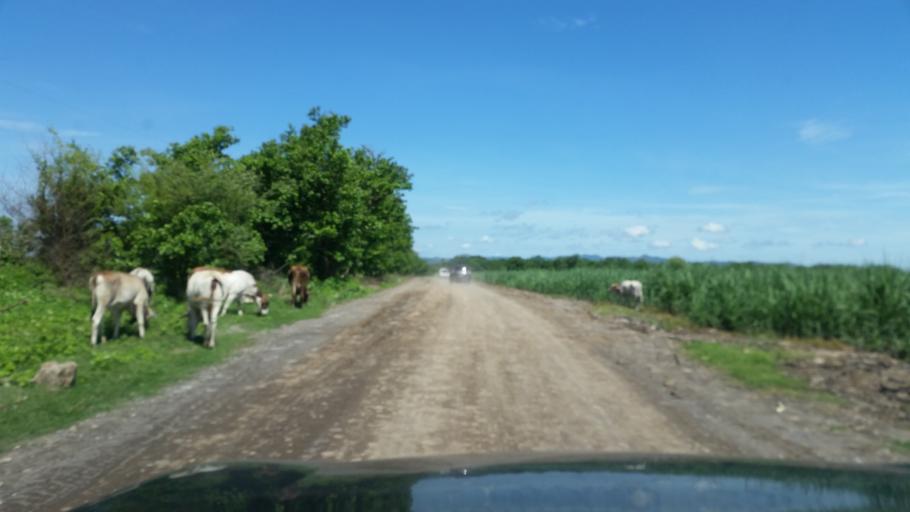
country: NI
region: Chinandega
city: Puerto Morazan
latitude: 12.7733
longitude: -87.1176
